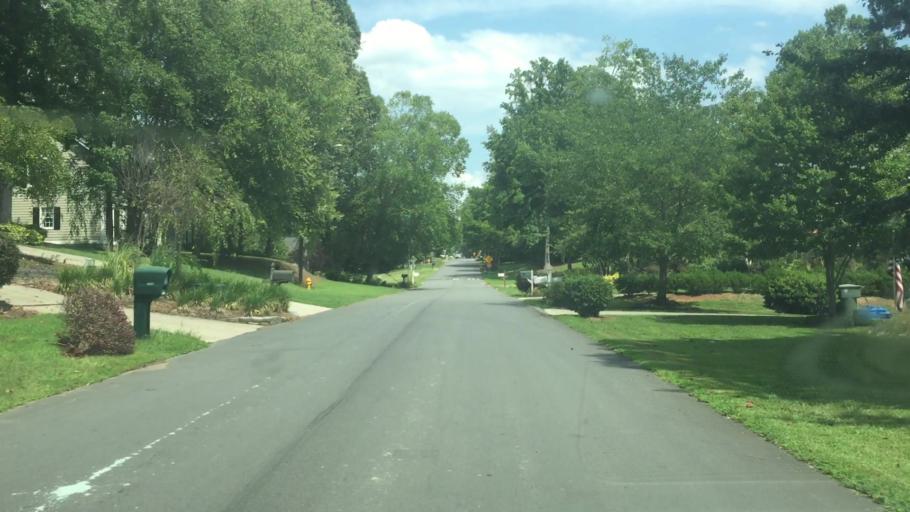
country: US
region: North Carolina
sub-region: Iredell County
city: Mooresville
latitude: 35.5520
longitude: -80.7964
